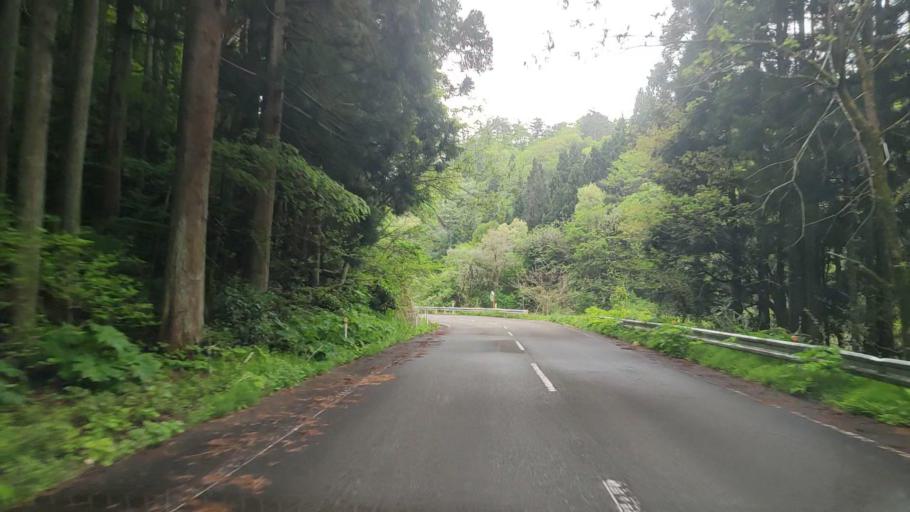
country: JP
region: Niigata
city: Gosen
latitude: 37.7101
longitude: 139.0954
